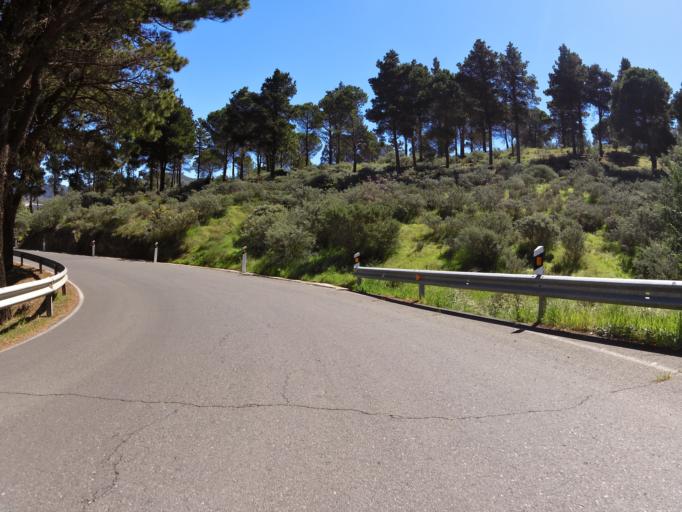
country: ES
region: Canary Islands
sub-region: Provincia de Las Palmas
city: Artenara
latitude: 28.0248
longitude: -15.6557
